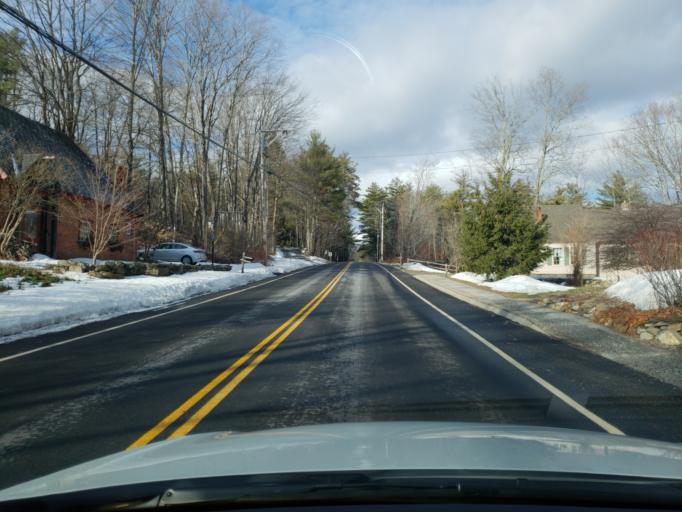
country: US
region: New Hampshire
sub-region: Hillsborough County
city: Greenfield
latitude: 42.9918
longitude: -71.8173
